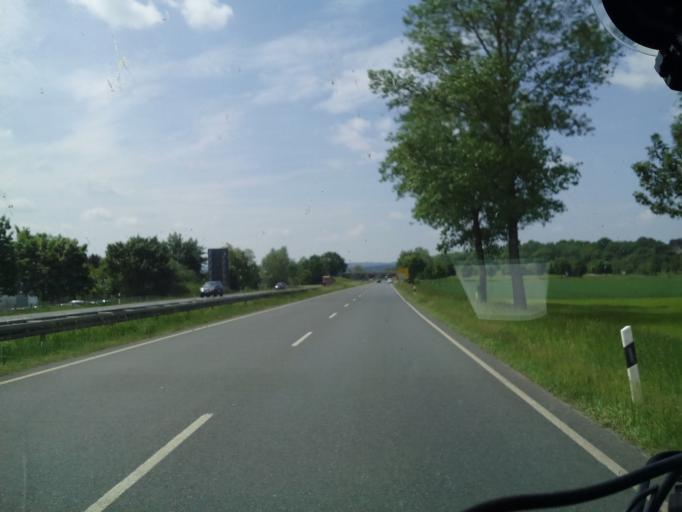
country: DE
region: Bavaria
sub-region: Upper Franconia
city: Kulmbach
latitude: 50.1059
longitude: 11.4253
